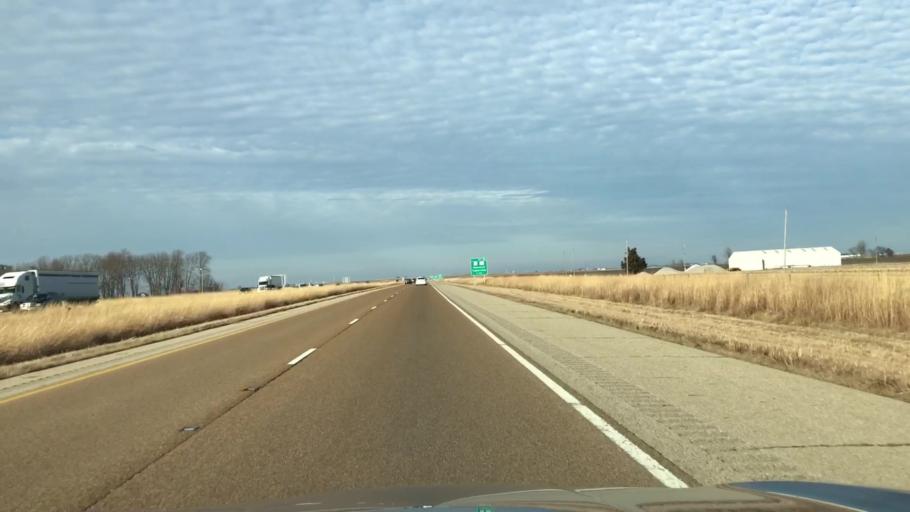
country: US
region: Illinois
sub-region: Montgomery County
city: Raymond
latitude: 39.3013
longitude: -89.6420
